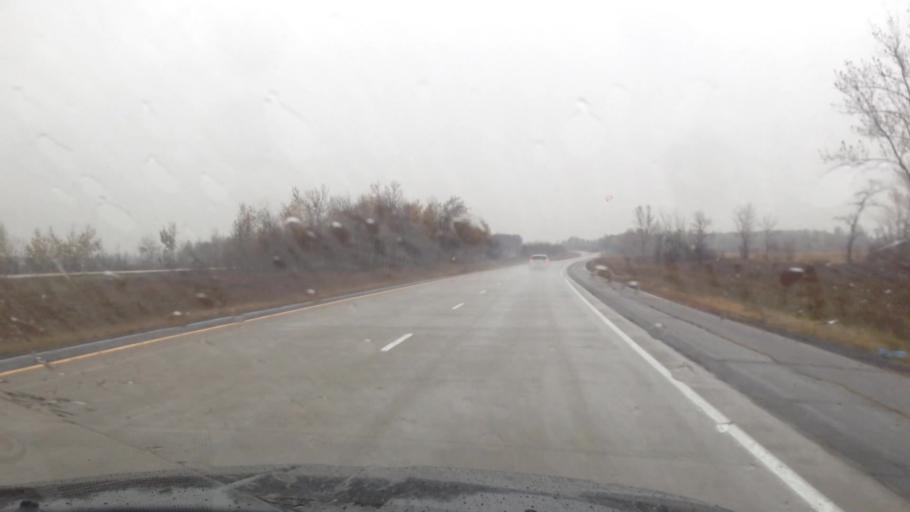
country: CA
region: Ontario
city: Hawkesbury
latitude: 45.4276
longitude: -74.7563
